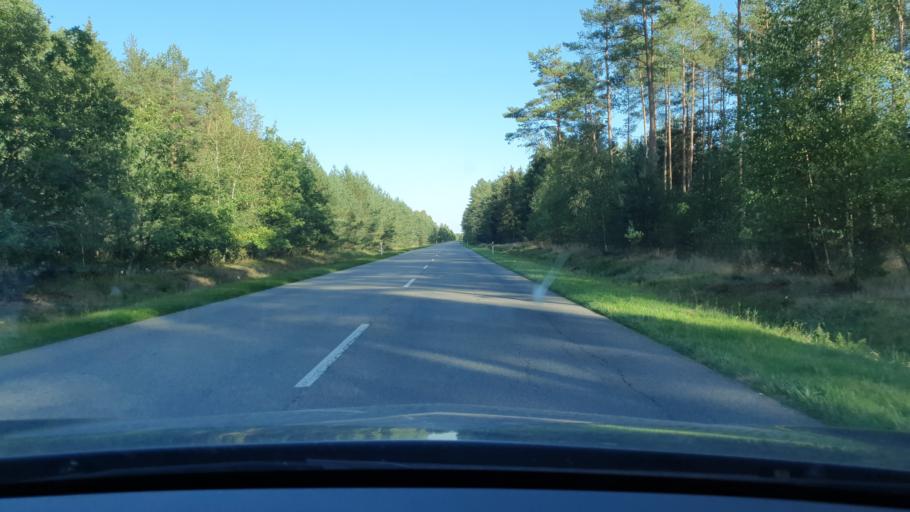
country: PL
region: West Pomeranian Voivodeship
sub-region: Powiat kamienski
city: Golczewo
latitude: 53.8124
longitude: 15.0998
